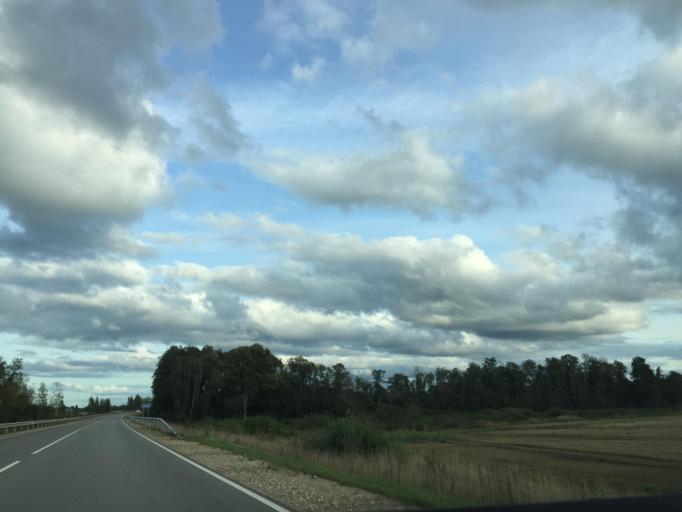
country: LV
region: Nereta
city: Nereta
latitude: 56.2477
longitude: 25.2440
